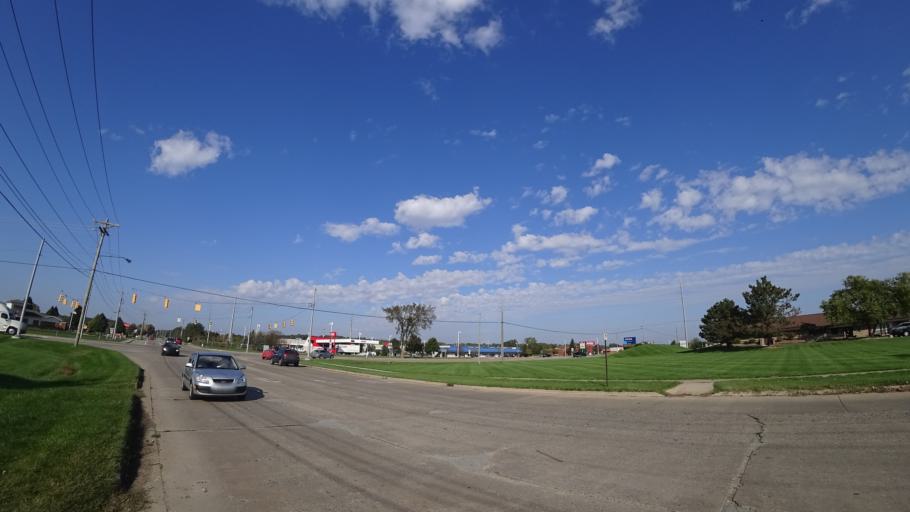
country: US
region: Michigan
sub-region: Saint Joseph County
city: Three Rivers
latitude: 41.9325
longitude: -85.6507
